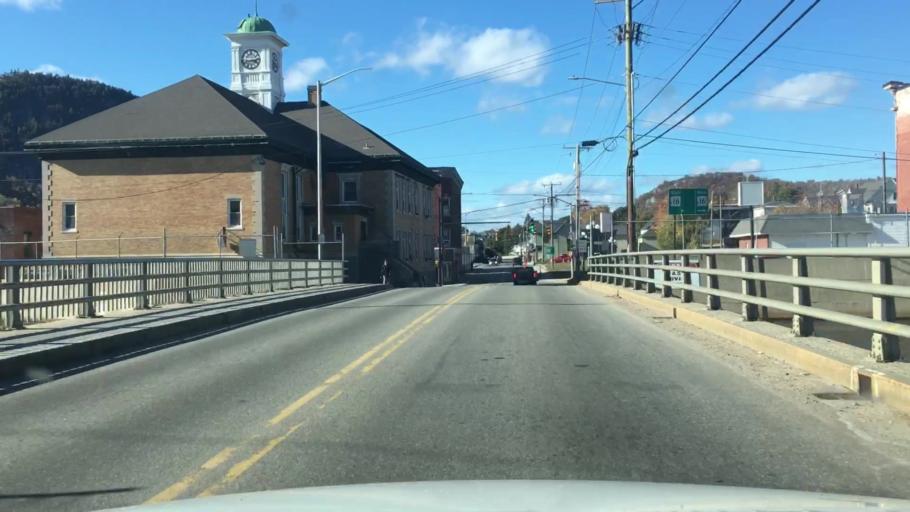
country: US
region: New Hampshire
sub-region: Coos County
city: Berlin
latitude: 44.4696
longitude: -71.1791
